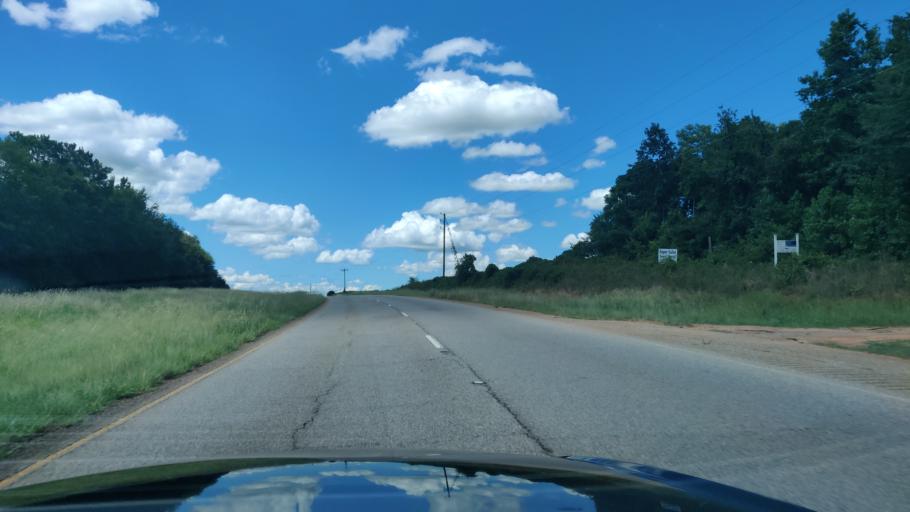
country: US
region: Georgia
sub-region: Stewart County
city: Richland
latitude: 32.0534
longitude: -84.6710
